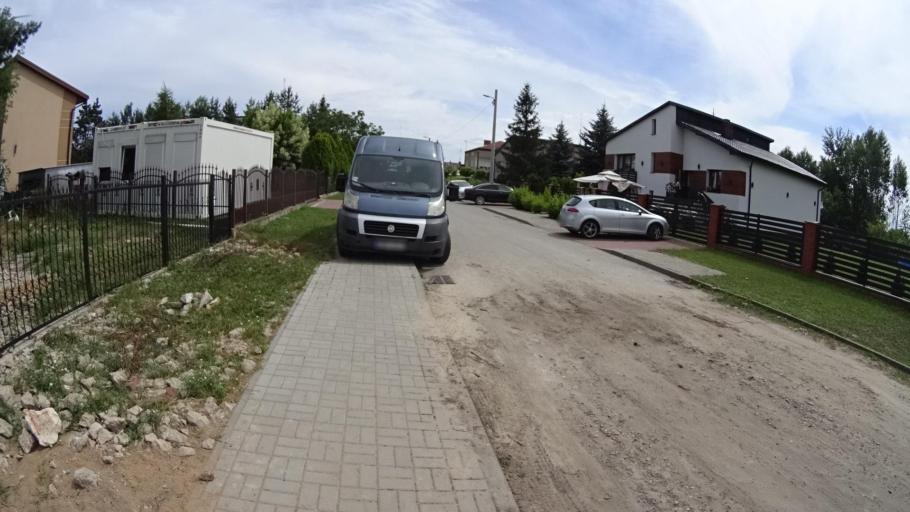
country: PL
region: Masovian Voivodeship
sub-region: Powiat bialobrzeski
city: Bialobrzegi
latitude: 51.6520
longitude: 20.9462
